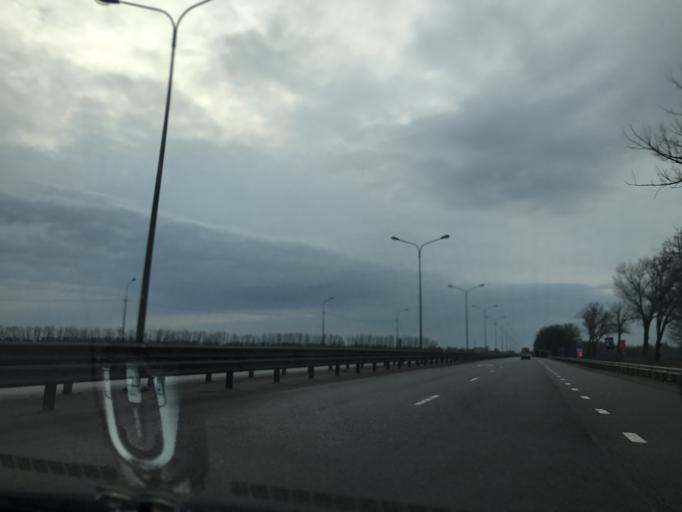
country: RU
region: Krasnodarskiy
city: Tikhoretsk
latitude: 45.8867
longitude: 40.1302
